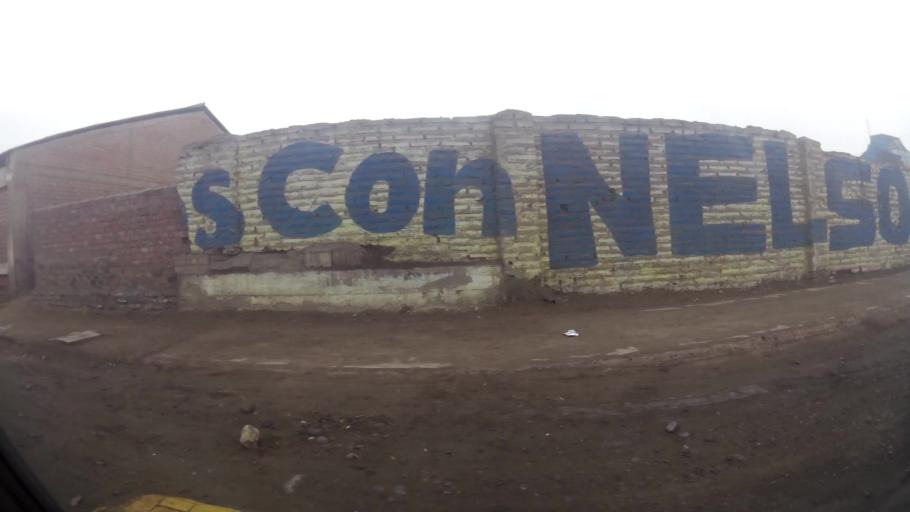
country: PE
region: Lima
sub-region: Provincia de Huaral
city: Chancay
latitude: -11.5812
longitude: -77.2693
